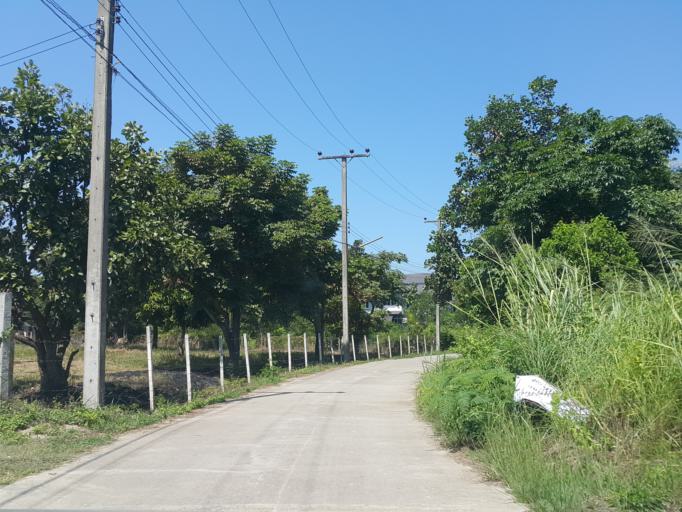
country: TH
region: Chiang Mai
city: Saraphi
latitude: 18.7630
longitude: 99.0598
